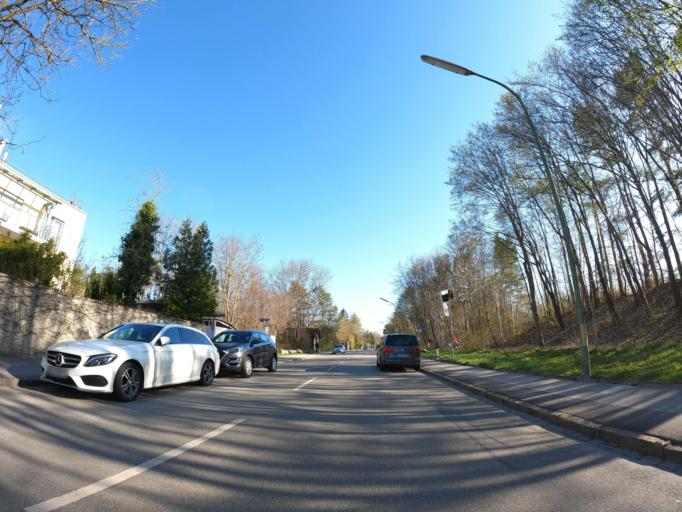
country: DE
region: Bavaria
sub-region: Upper Bavaria
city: Ottobrunn
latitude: 48.0669
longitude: 11.6533
